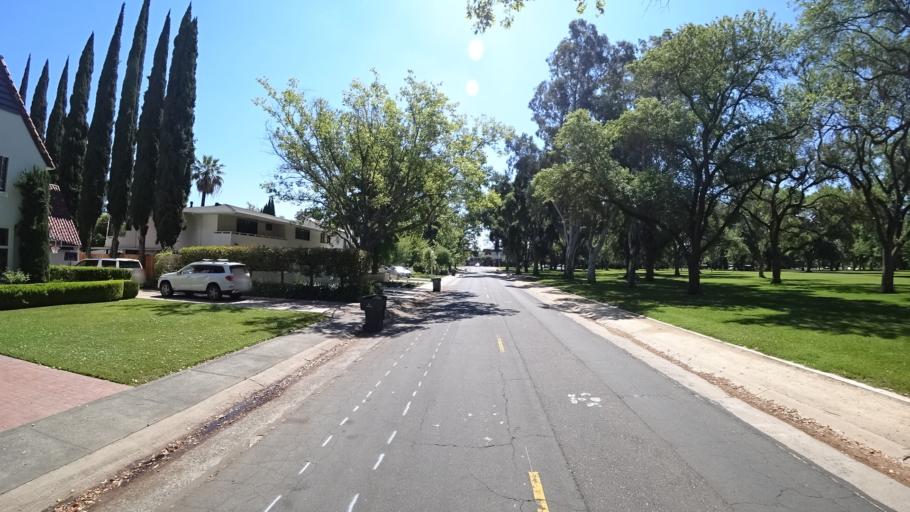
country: US
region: California
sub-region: Sacramento County
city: Sacramento
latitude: 38.5426
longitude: -121.4937
